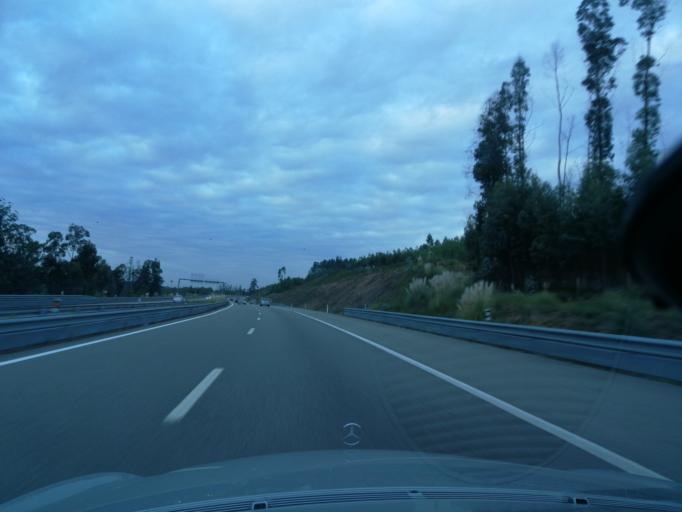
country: PT
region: Aveiro
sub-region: Estarreja
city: Salreu
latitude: 40.6973
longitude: -8.5336
